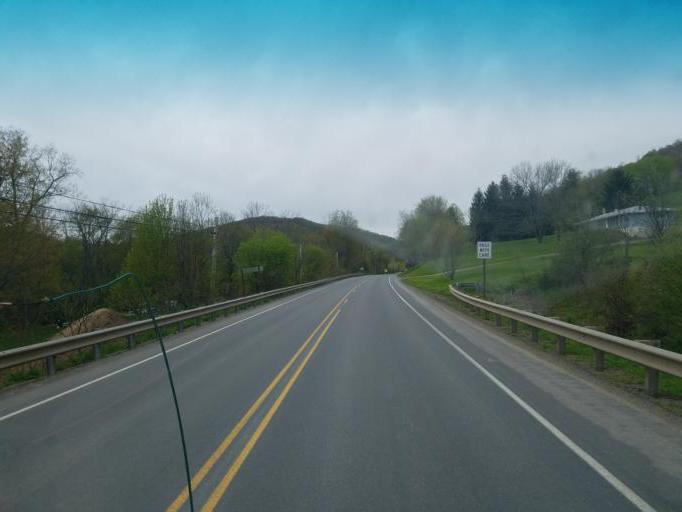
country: US
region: Pennsylvania
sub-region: Tioga County
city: Westfield
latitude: 41.9148
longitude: -77.6110
